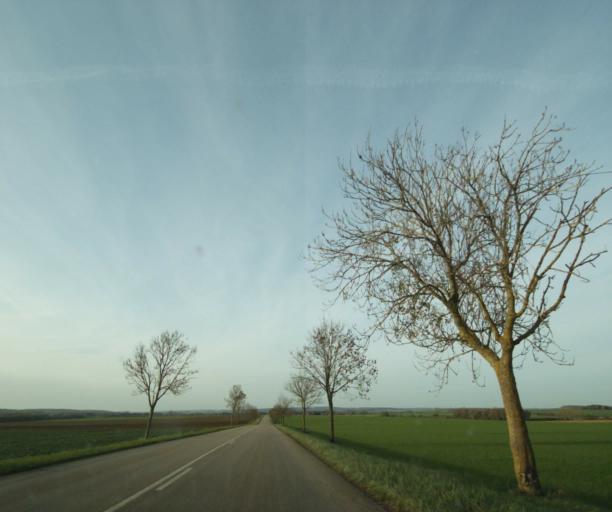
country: FR
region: Lorraine
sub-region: Departement de Meurthe-et-Moselle
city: Pierrepont
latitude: 49.3398
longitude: 5.6565
